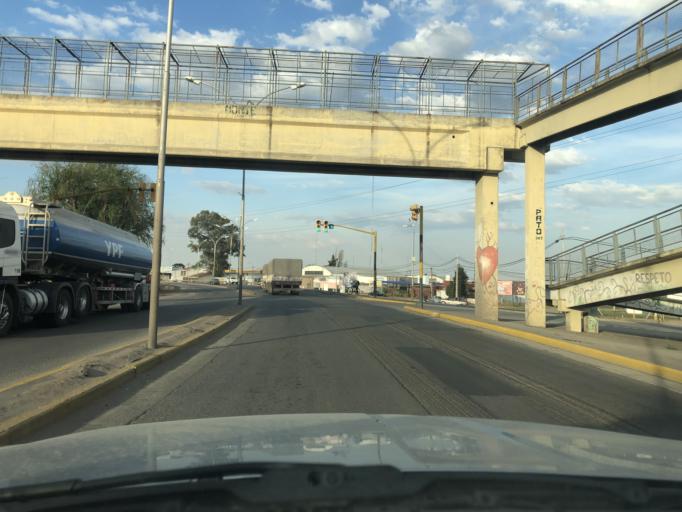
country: AR
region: Cordoba
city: Jesus Maria
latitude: -30.9874
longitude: -64.0906
